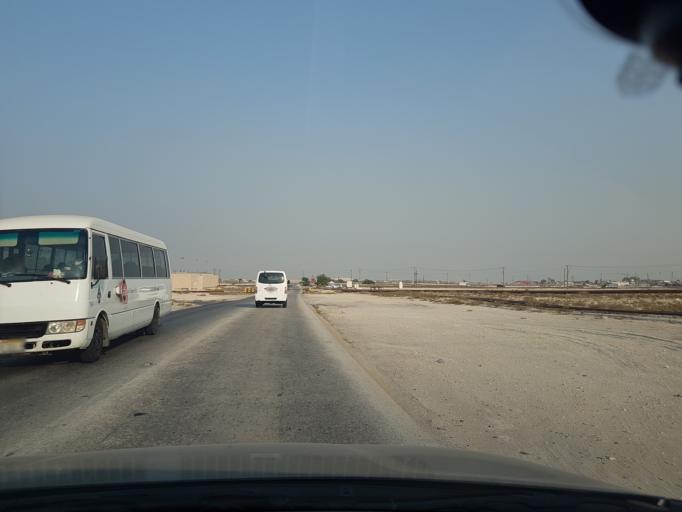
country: BH
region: Northern
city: Ar Rifa'
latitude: 26.0899
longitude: 50.5691
